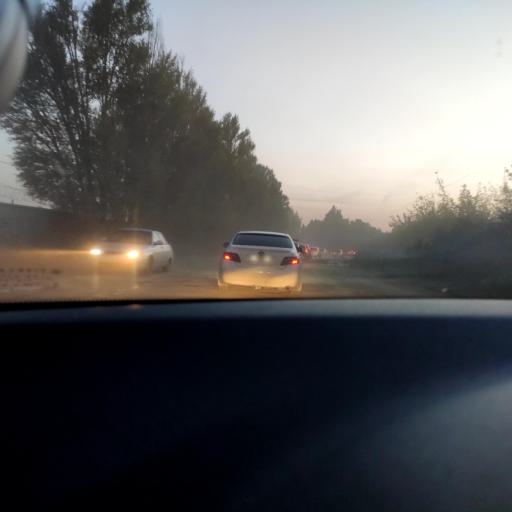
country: RU
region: Samara
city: Novosemeykino
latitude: 53.3568
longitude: 50.3517
